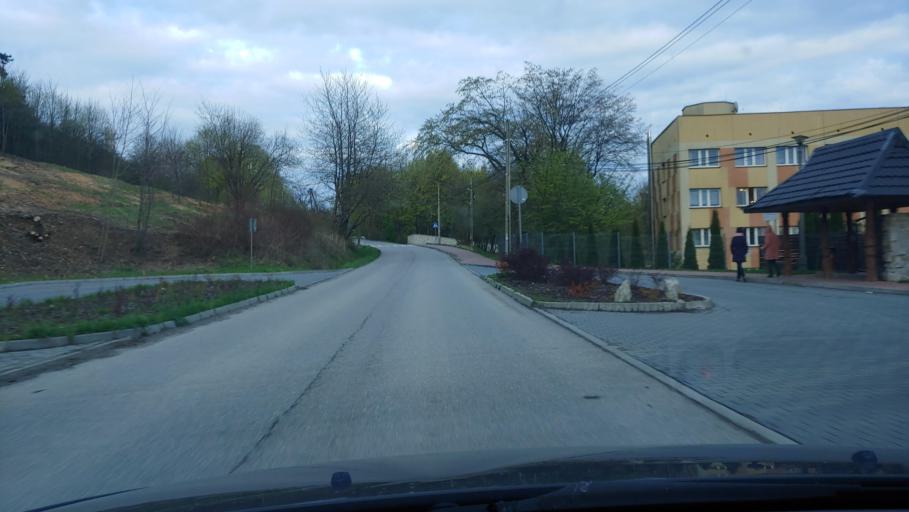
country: PL
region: Lesser Poland Voivodeship
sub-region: Powiat krakowski
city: Bolechowice
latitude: 50.1525
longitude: 19.7735
